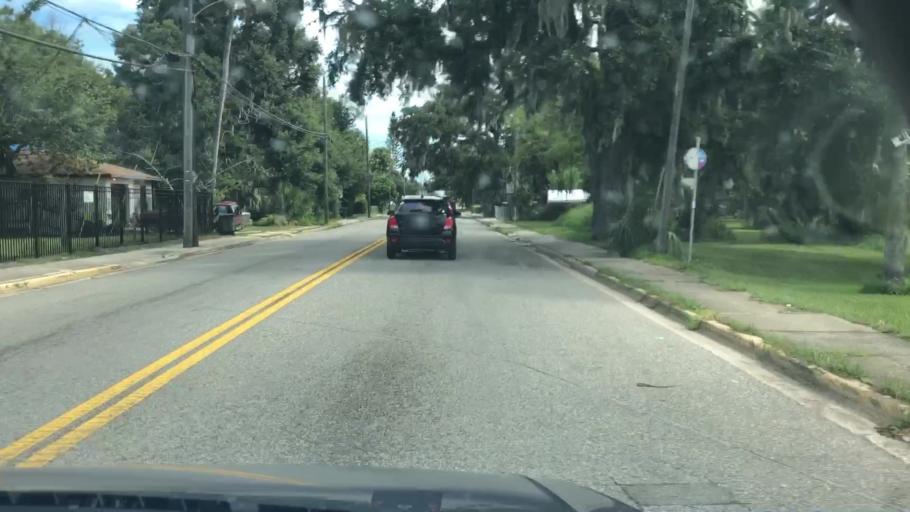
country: US
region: Florida
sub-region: Volusia County
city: Daytona Beach
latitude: 29.1951
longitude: -81.0212
